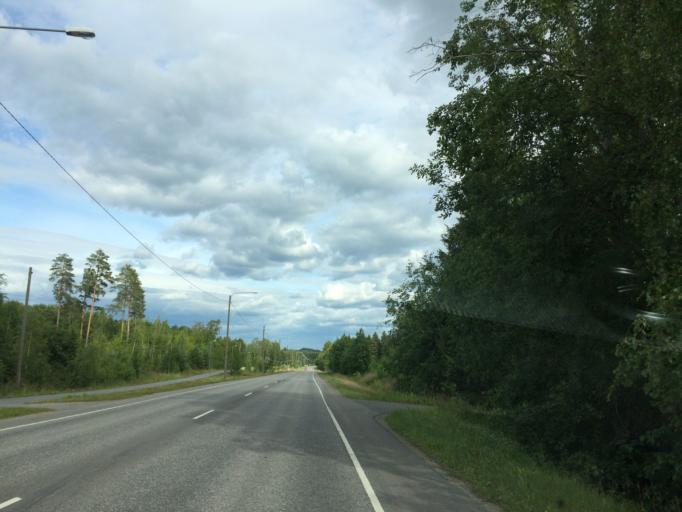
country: FI
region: Haeme
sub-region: Haemeenlinna
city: Janakkala
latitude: 60.9607
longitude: 24.5683
